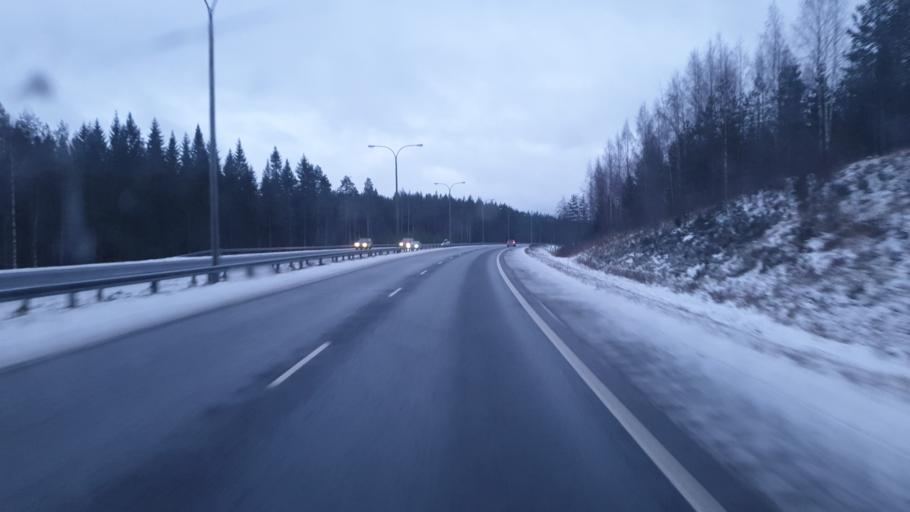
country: FI
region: Northern Savo
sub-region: Kuopio
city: Siilinjaervi
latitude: 63.0117
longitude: 27.6767
